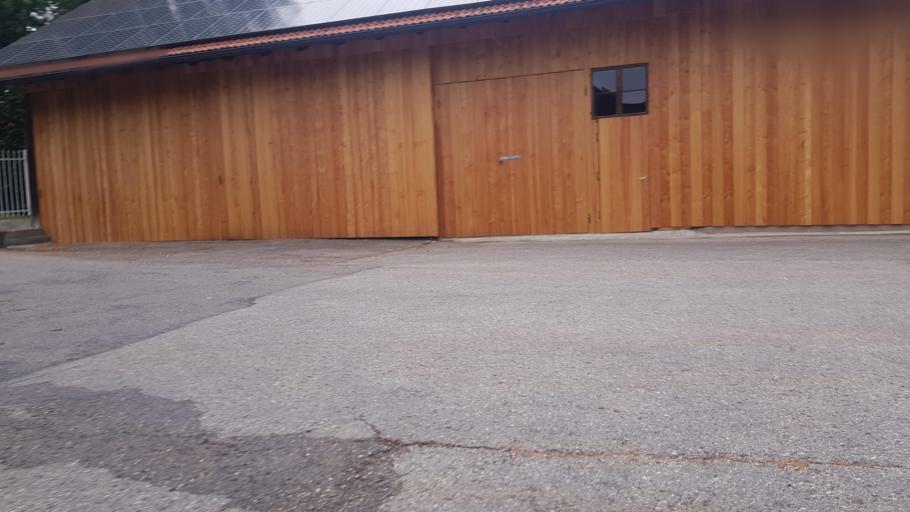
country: DE
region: Bavaria
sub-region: Upper Bavaria
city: Starnberg
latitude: 48.0248
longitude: 11.3486
